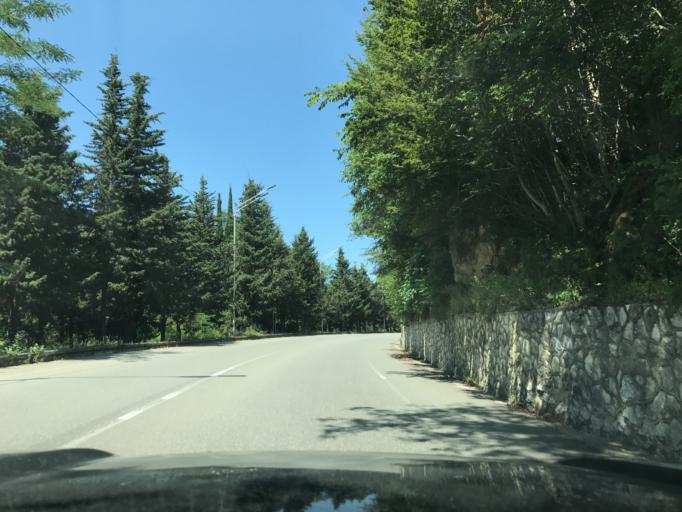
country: GE
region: Abkhazia
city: Gagra
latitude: 43.2812
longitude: 40.2771
